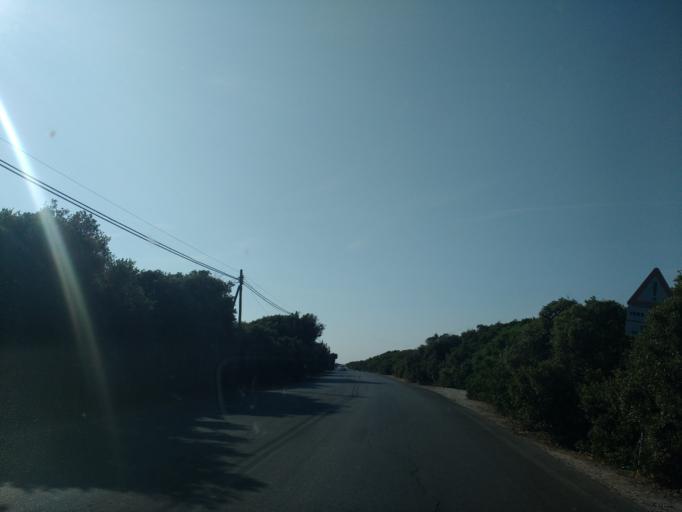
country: IT
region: Latium
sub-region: Citta metropolitana di Roma Capitale
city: Torvaianica
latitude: 41.6792
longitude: 12.3861
